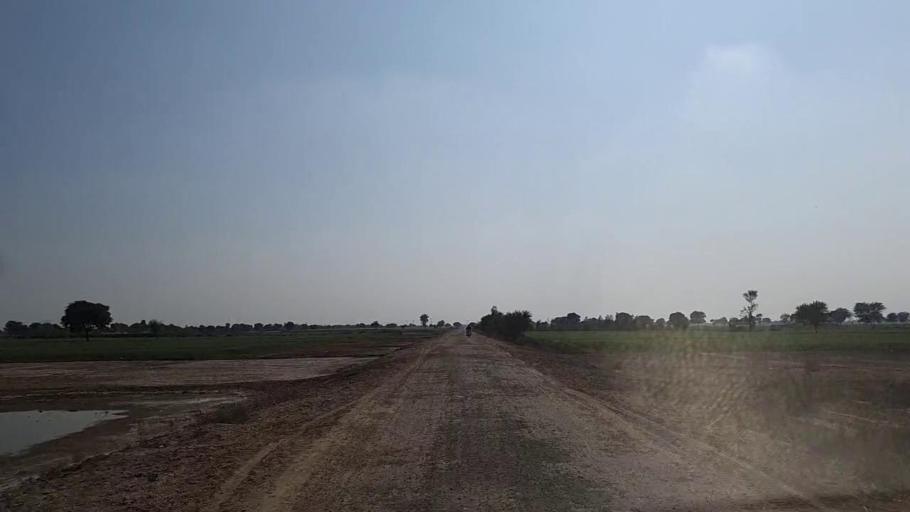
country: PK
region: Sindh
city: Jam Sahib
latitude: 26.2671
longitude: 68.5672
